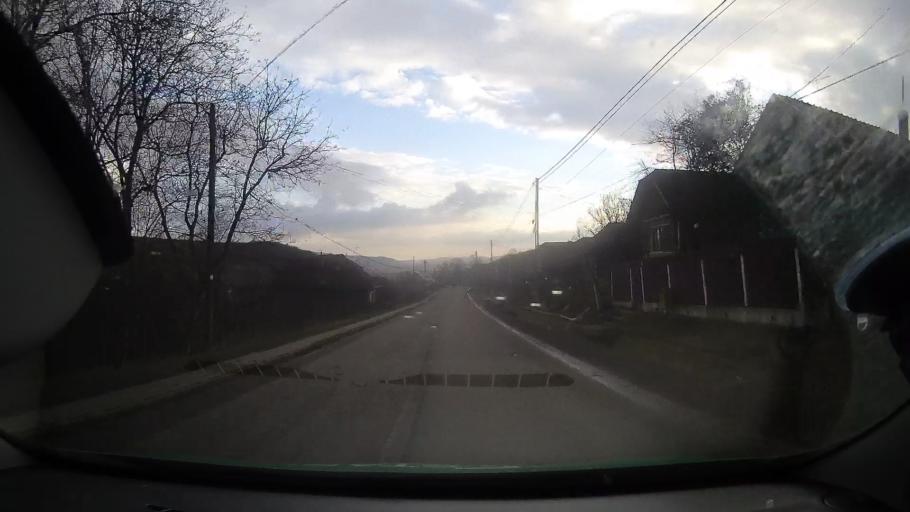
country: RO
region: Alba
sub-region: Comuna Lunca Muresului
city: Lunca Muresului
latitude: 46.4347
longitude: 23.9087
